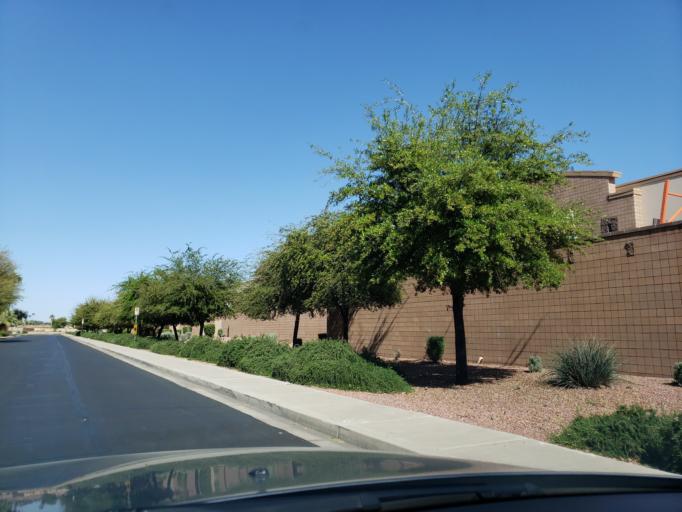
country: US
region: Arizona
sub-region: Maricopa County
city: Glendale
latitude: 33.5834
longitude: -112.1890
